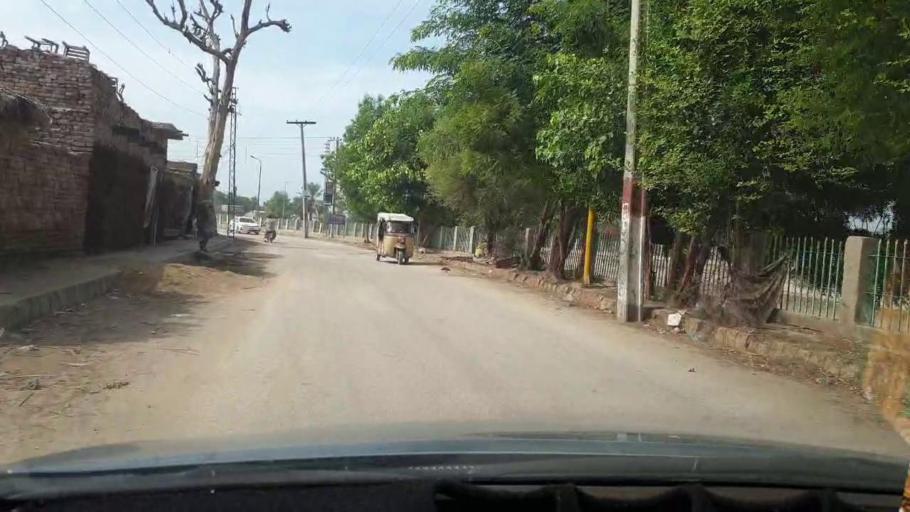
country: PK
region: Sindh
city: Khairpur
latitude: 27.5317
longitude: 68.7531
